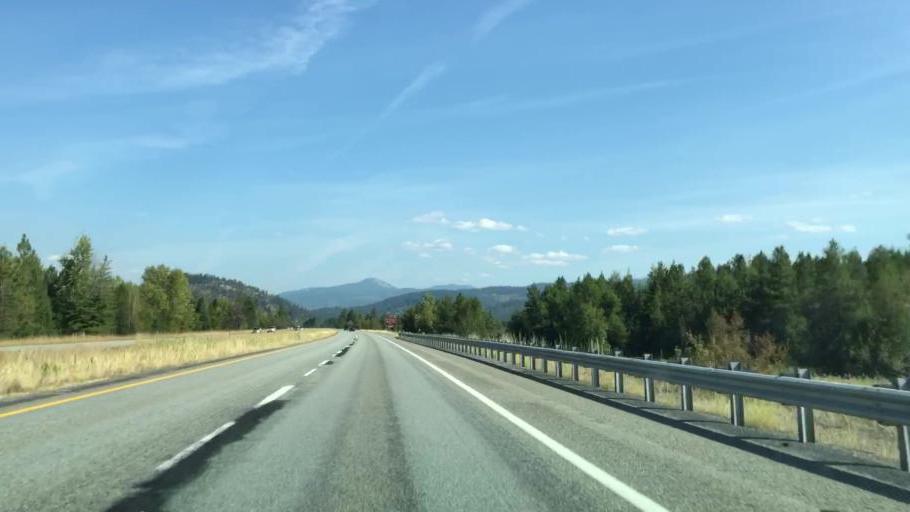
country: US
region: Idaho
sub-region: Shoshone County
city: Pinehurst
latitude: 47.5573
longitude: -116.3857
